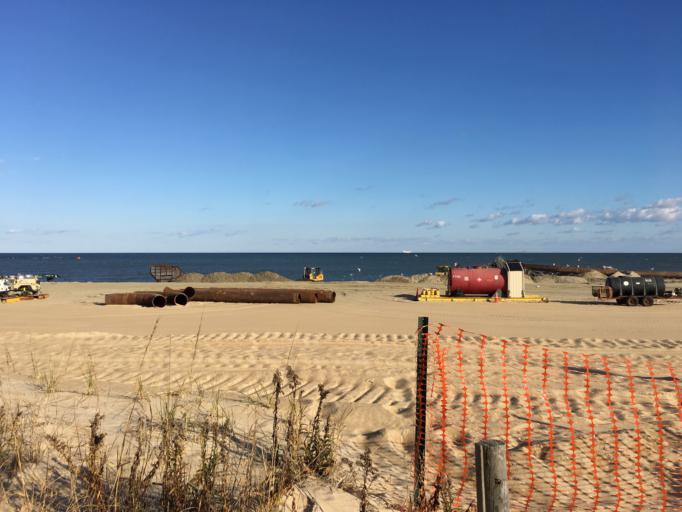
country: US
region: Delaware
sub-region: Sussex County
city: Rehoboth Beach
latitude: 38.7196
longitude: -75.0765
